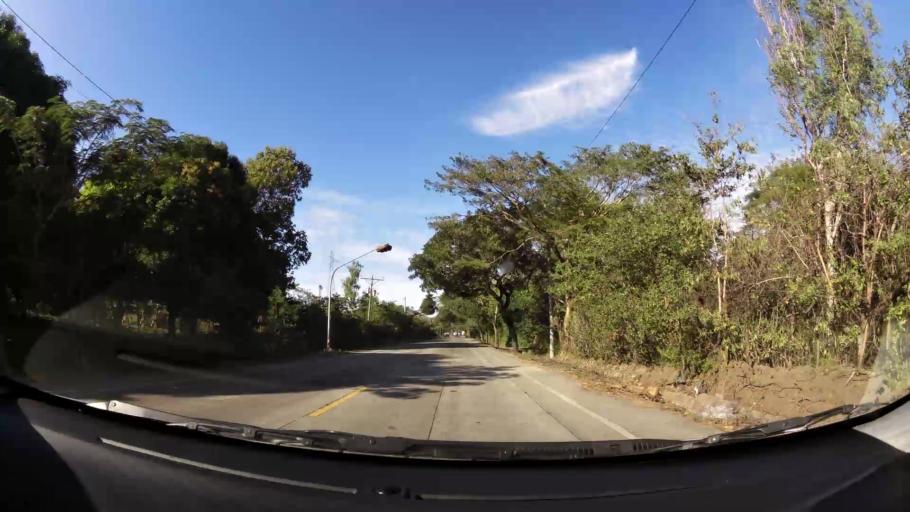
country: SV
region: Santa Ana
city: Texistepeque
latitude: 14.1038
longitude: -89.4999
